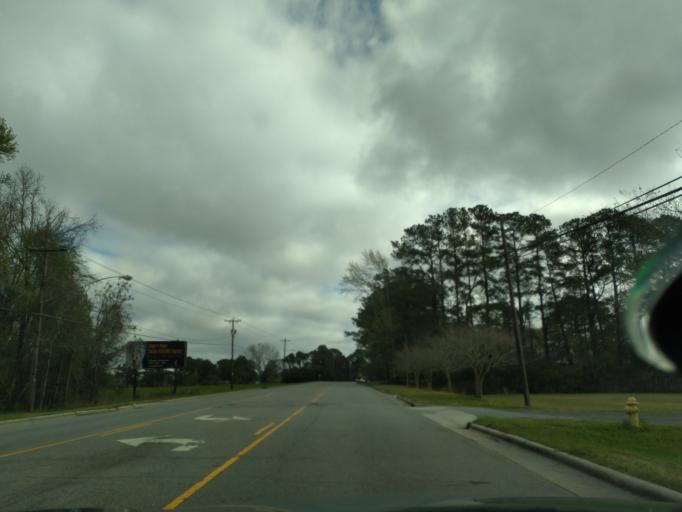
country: US
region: North Carolina
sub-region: Chowan County
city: Edenton
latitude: 36.0599
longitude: -76.6231
